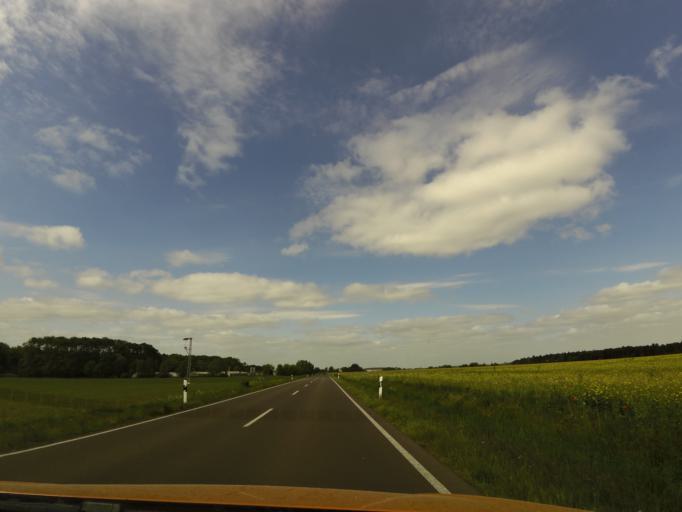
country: DE
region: Saxony-Anhalt
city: Loburg
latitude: 52.1095
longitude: 12.1432
